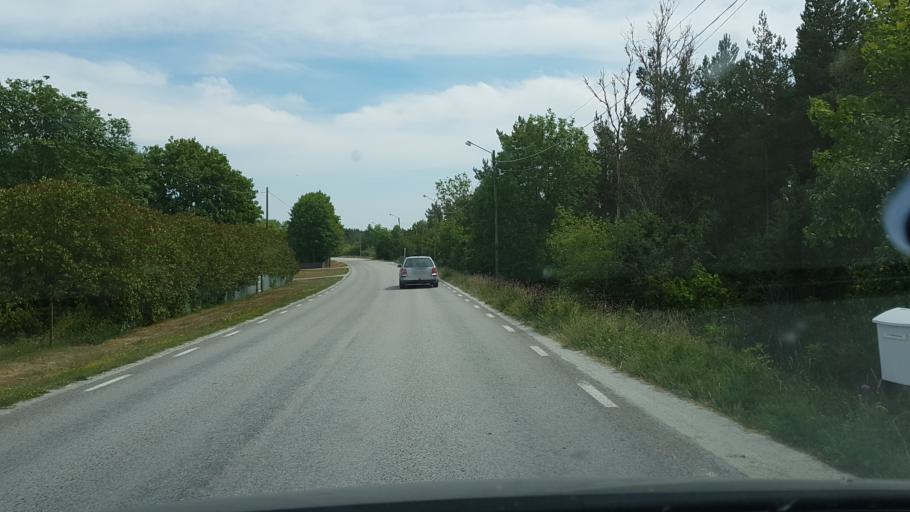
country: SE
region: Gotland
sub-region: Gotland
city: Slite
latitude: 57.7315
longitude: 18.7423
